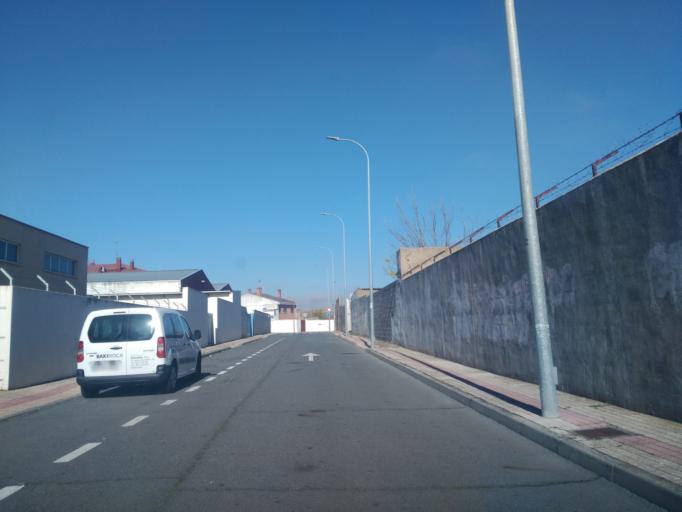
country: ES
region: Castille and Leon
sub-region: Provincia de Salamanca
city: Santa Marta de Tormes
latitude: 40.9729
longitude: -5.6375
